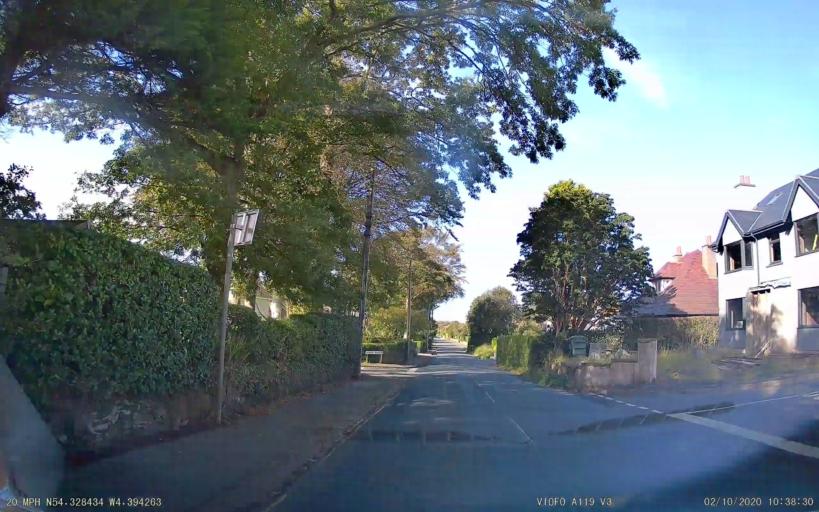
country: IM
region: Ramsey
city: Ramsey
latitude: 54.3284
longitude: -4.3943
